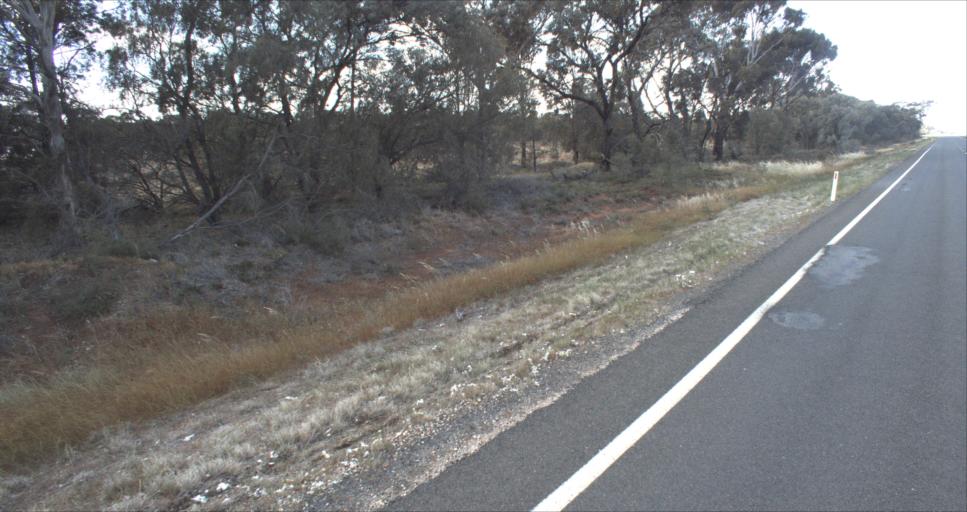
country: AU
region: New South Wales
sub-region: Murrumbidgee Shire
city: Darlington Point
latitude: -34.5362
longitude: 146.1730
